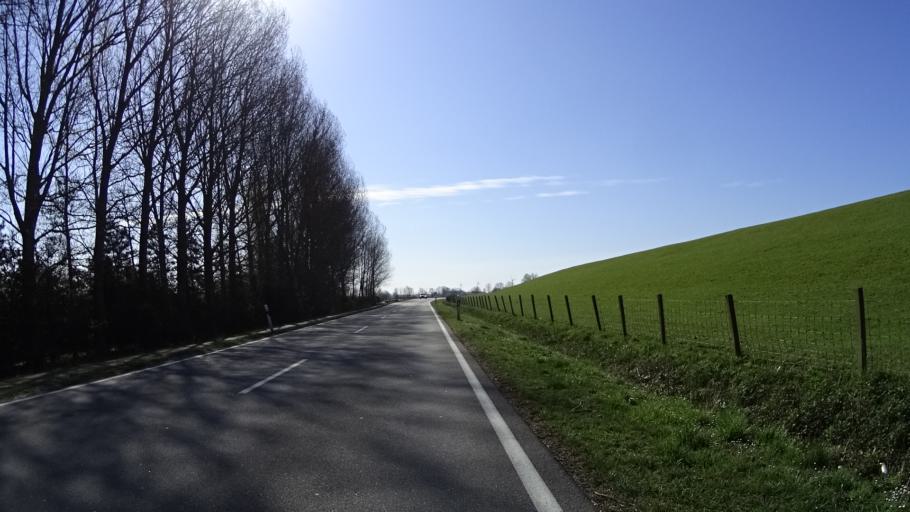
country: DE
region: Lower Saxony
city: Jemgum
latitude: 53.2895
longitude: 7.4032
